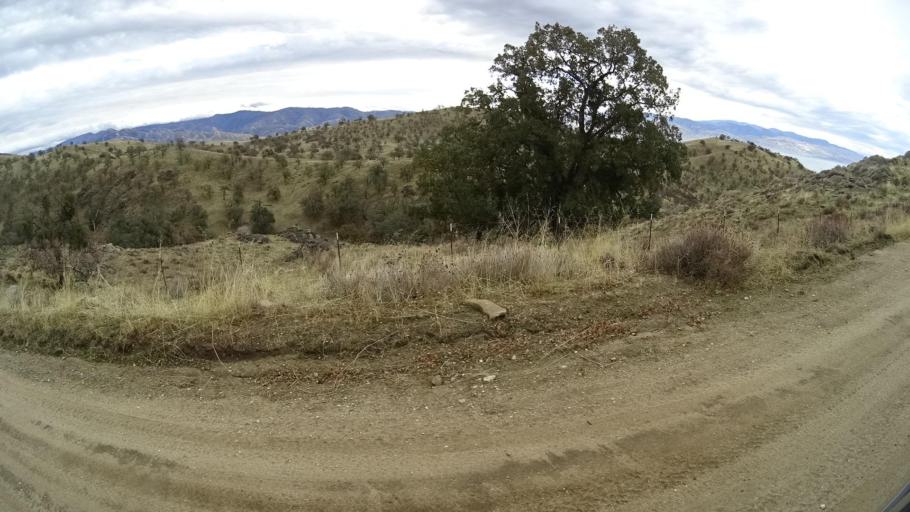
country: US
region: California
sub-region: Kern County
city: Stallion Springs
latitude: 35.1234
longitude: -118.7403
